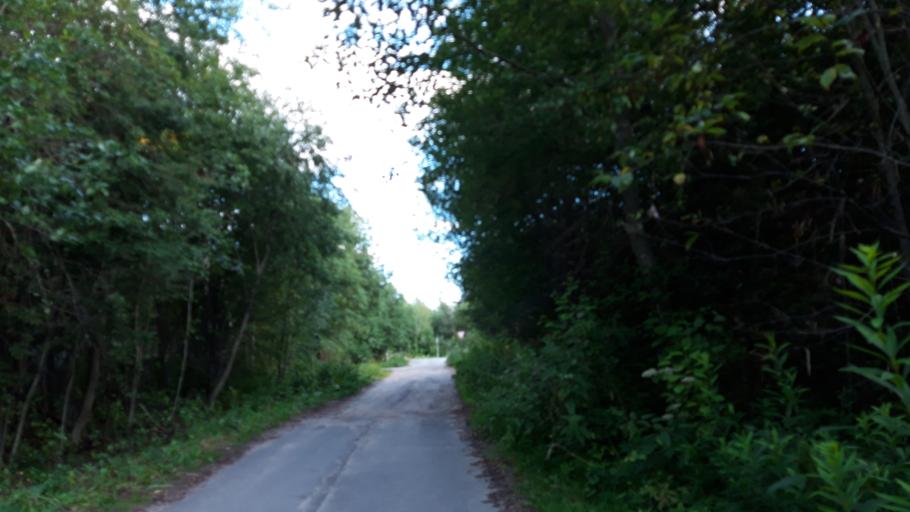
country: RU
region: Tverskaya
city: Konakovo
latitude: 56.6721
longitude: 36.7306
